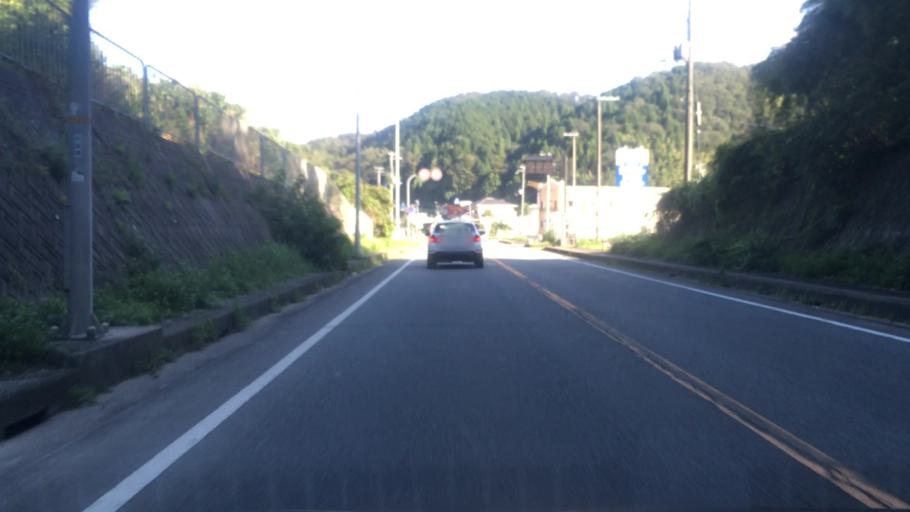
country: JP
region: Hyogo
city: Toyooka
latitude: 35.5559
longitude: 134.8328
